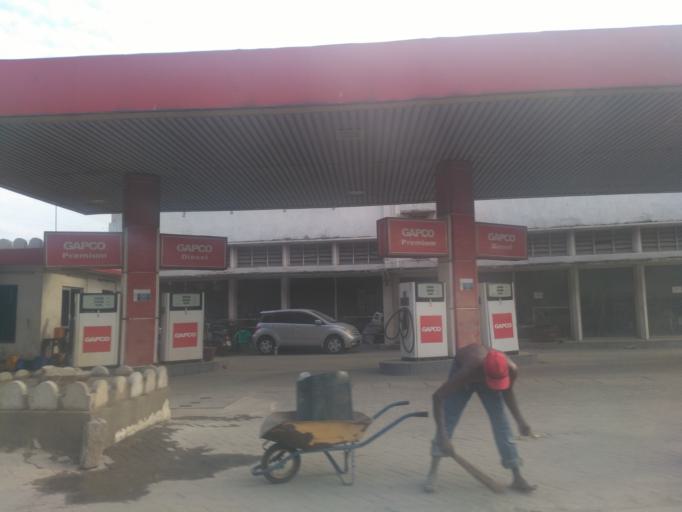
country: TZ
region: Zanzibar Urban/West
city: Zanzibar
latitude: -6.1578
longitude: 39.1952
